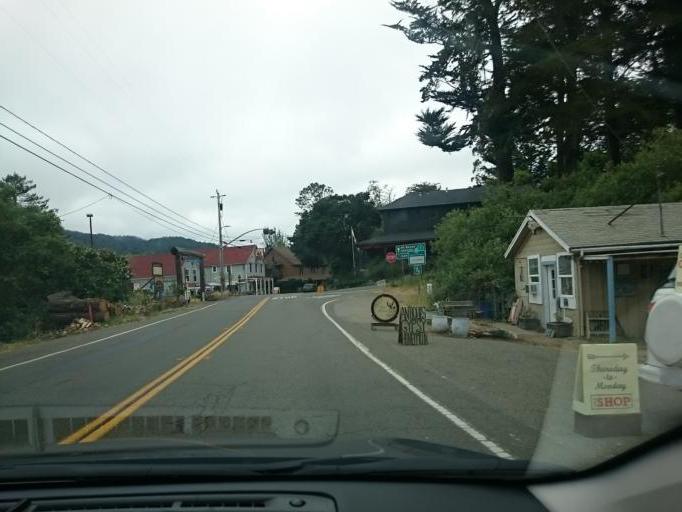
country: US
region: California
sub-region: Marin County
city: Inverness
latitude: 38.0403
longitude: -122.7872
